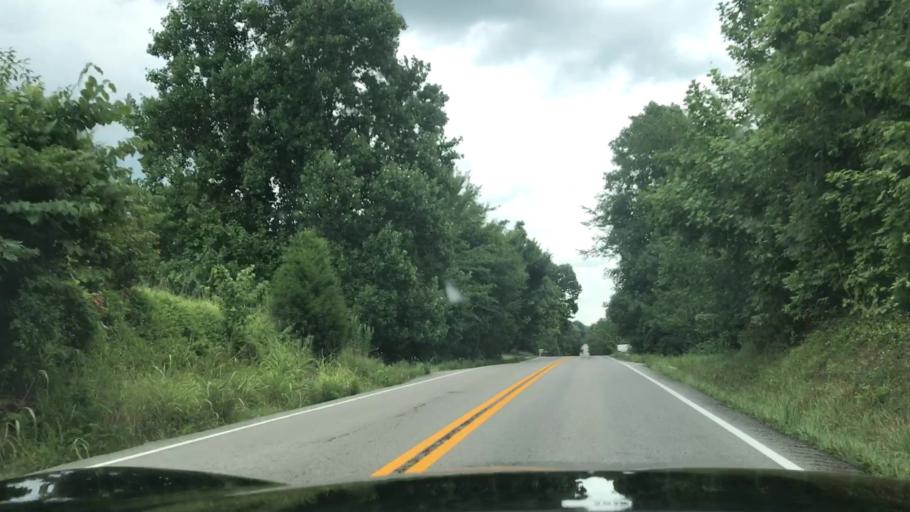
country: US
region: Kentucky
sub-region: Muhlenberg County
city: Central City
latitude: 37.2021
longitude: -86.9614
